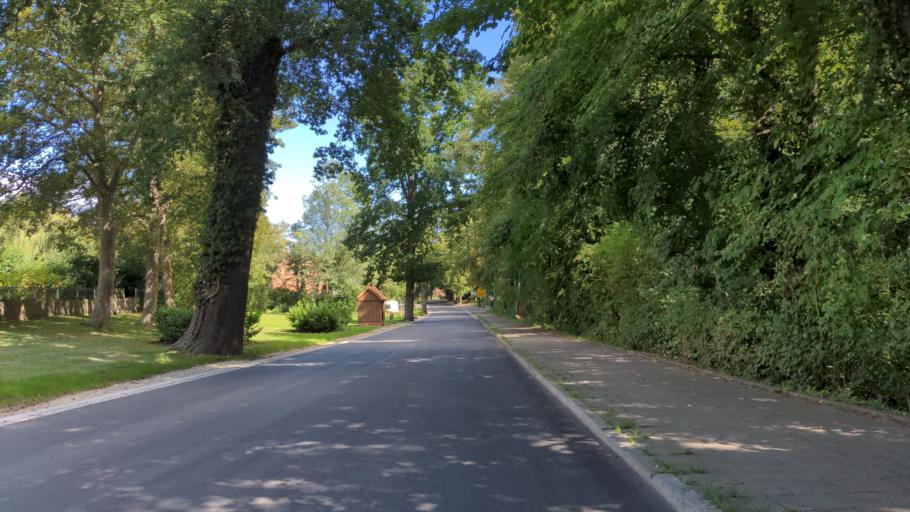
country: DE
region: Schleswig-Holstein
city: Lensahn
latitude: 54.2169
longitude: 10.8753
